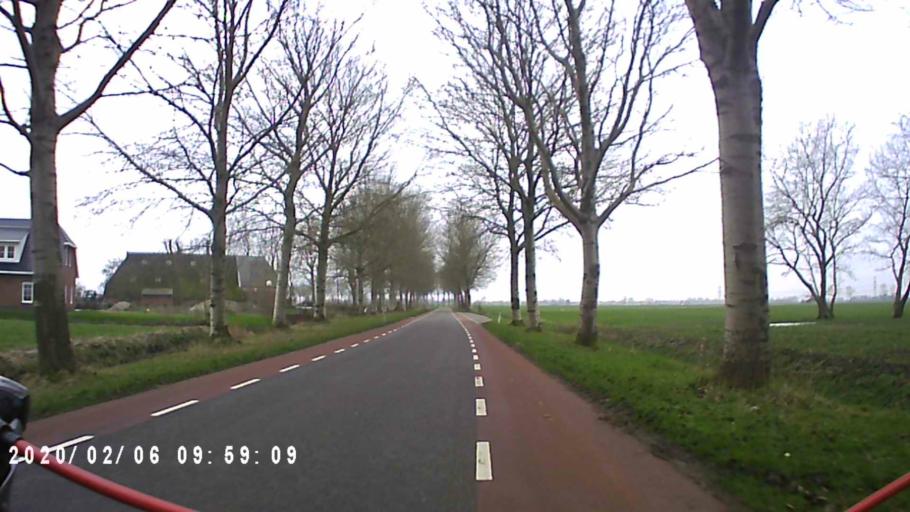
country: NL
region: Groningen
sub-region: Gemeente Zuidhorn
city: Aduard
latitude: 53.2692
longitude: 6.4946
